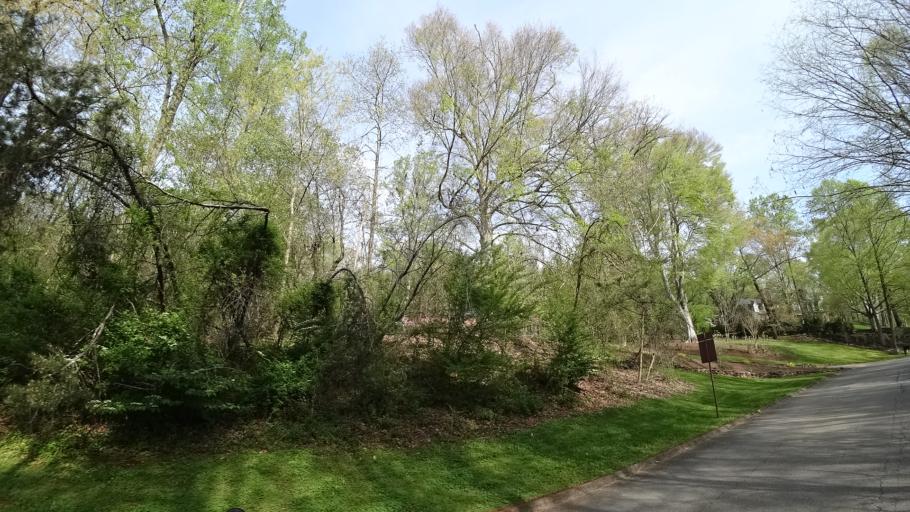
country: US
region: Tennessee
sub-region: Knox County
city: Knoxville
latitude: 35.9064
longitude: -83.9850
